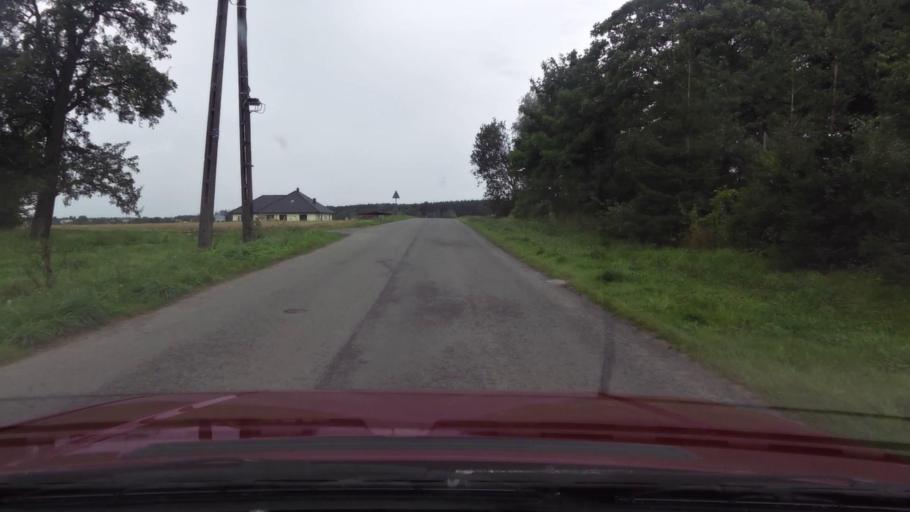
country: PL
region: West Pomeranian Voivodeship
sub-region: Powiat kolobrzeski
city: Grzybowo
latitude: 54.1471
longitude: 15.5094
